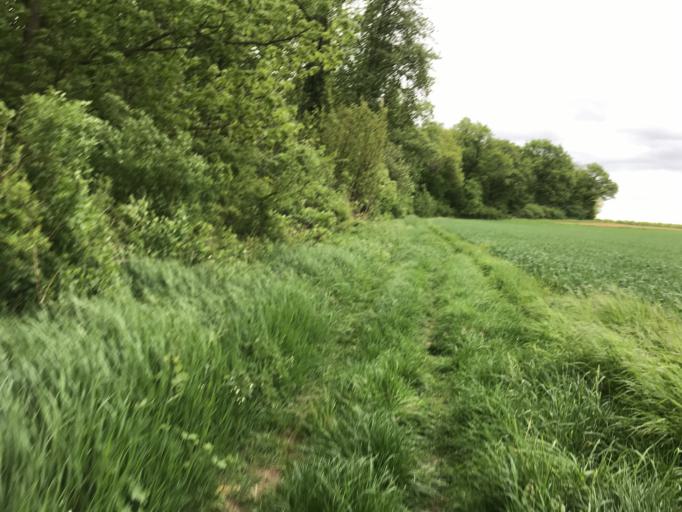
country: DE
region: Rheinland-Pfalz
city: Ober-Olm
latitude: 49.9508
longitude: 8.1723
